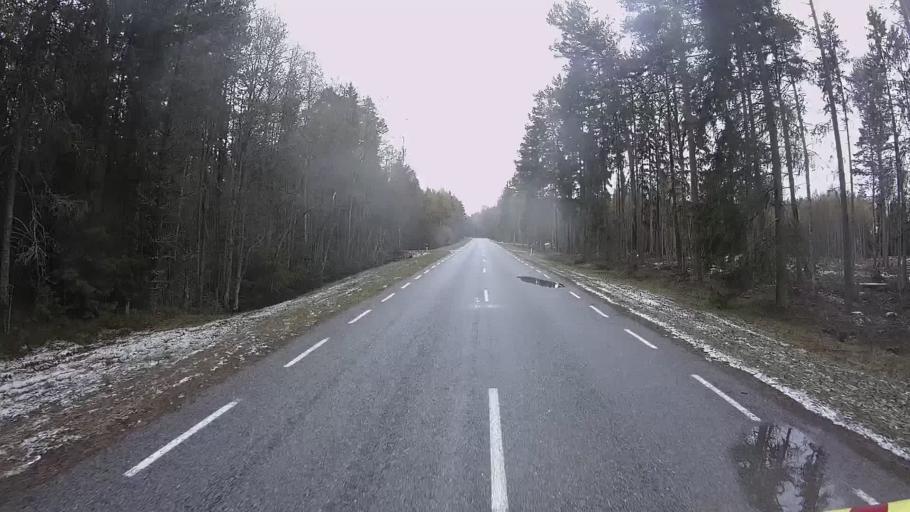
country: EE
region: Hiiumaa
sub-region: Kaerdla linn
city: Kardla
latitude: 59.0452
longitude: 22.6814
